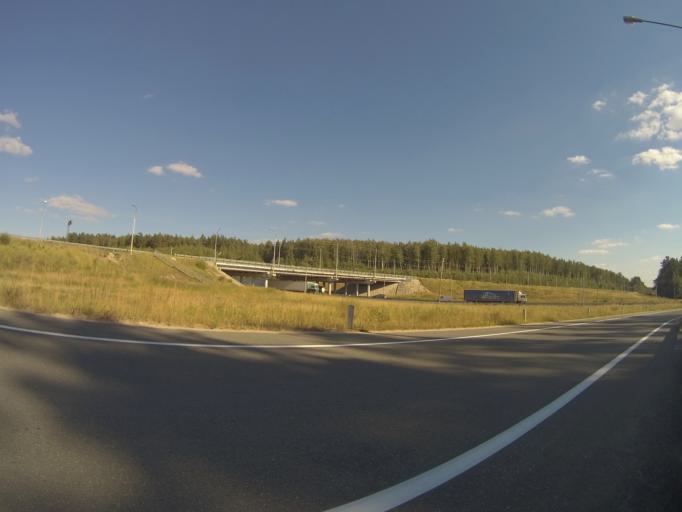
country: RU
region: Vladimir
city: Kommunar
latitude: 56.0571
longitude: 40.4382
